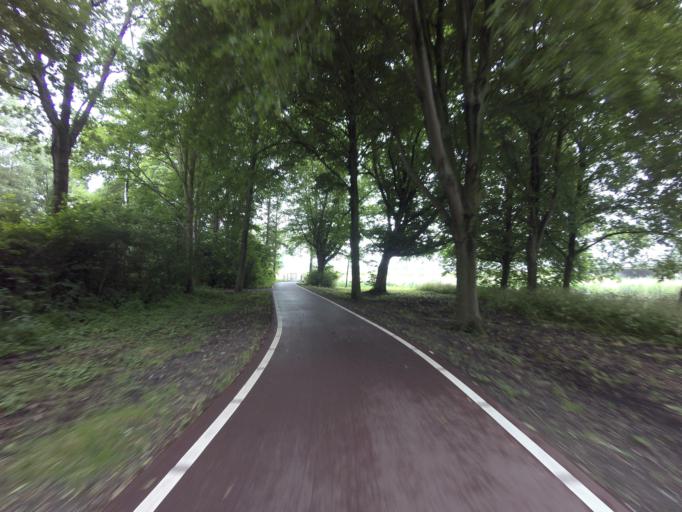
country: NL
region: North Holland
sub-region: Gemeente Purmerend
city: Purmerend
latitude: 52.5276
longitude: 4.9580
